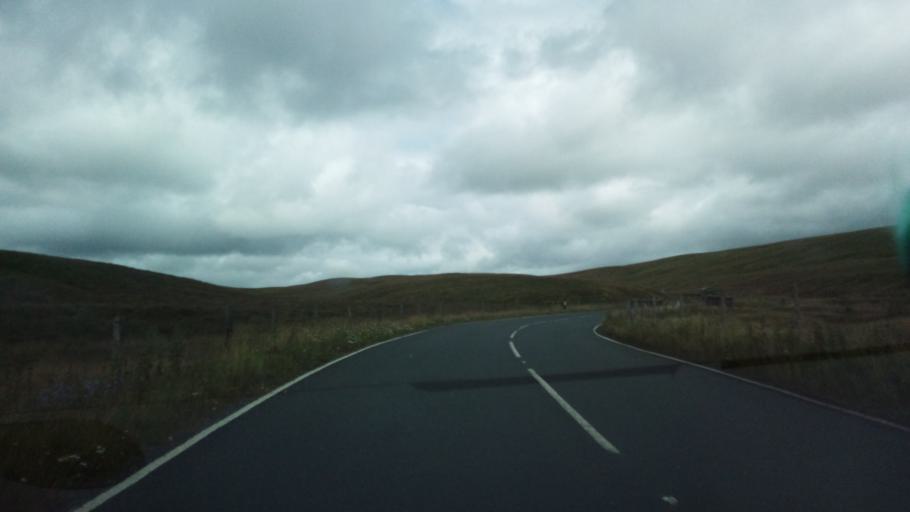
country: GB
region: England
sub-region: North Yorkshire
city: Settle
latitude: 54.2327
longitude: -2.3186
